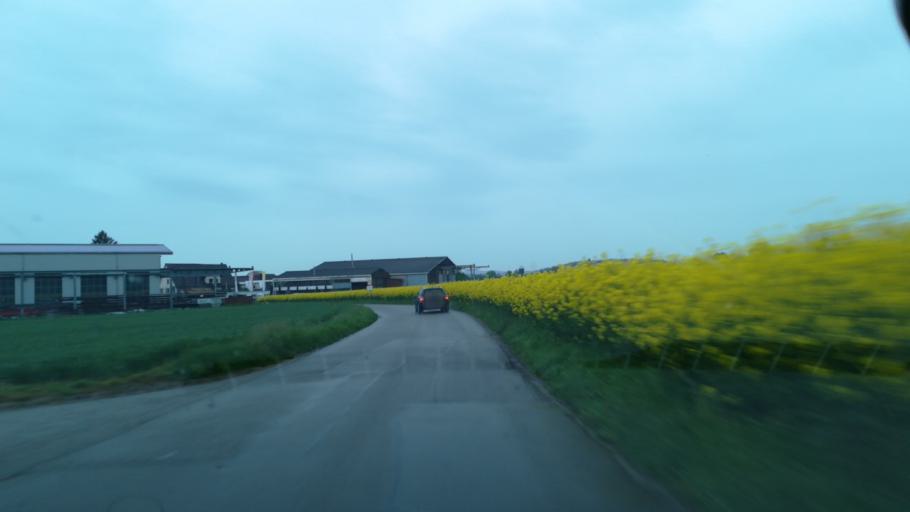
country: CH
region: Zurich
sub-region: Bezirk Buelach
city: End-Hoeri
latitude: 47.5115
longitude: 8.5021
